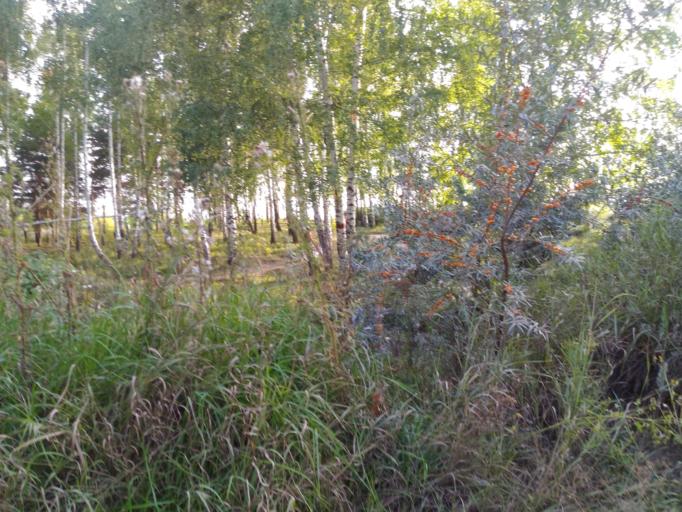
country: RU
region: Ulyanovsk
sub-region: Ulyanovskiy Rayon
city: Ulyanovsk
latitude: 54.3576
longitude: 48.5150
